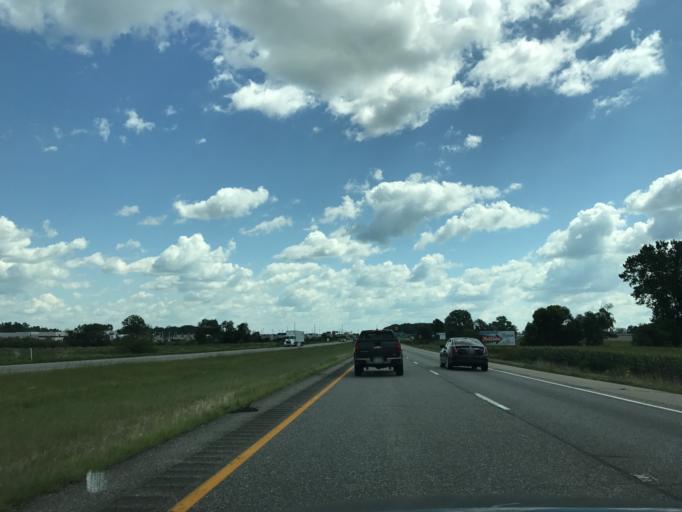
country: US
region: Indiana
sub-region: Marshall County
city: Plymouth
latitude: 41.3614
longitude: -86.3375
